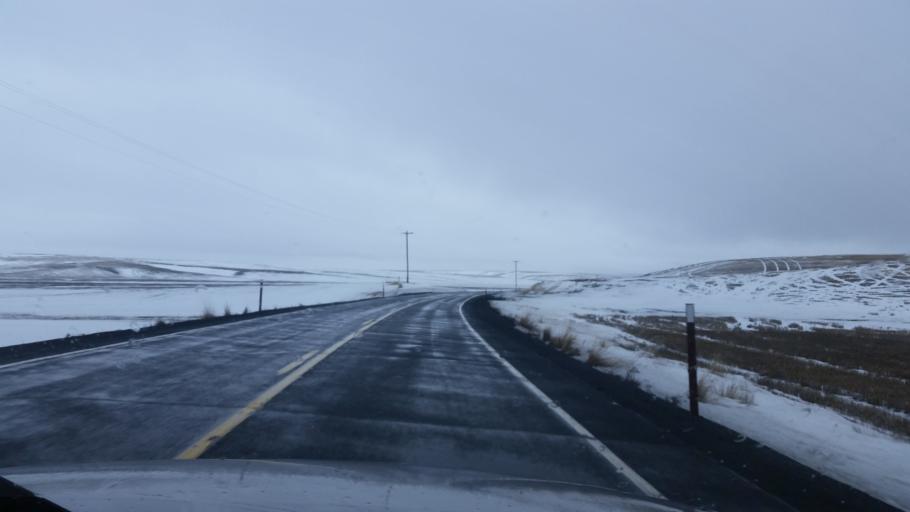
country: US
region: Washington
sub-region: Lincoln County
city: Davenport
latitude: 47.4767
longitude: -118.1895
